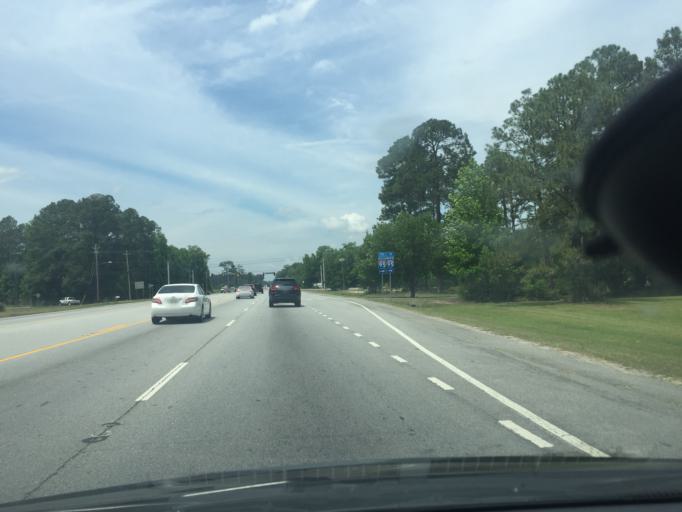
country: US
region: Georgia
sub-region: Chatham County
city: Bloomingdale
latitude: 32.1349
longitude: -81.3067
